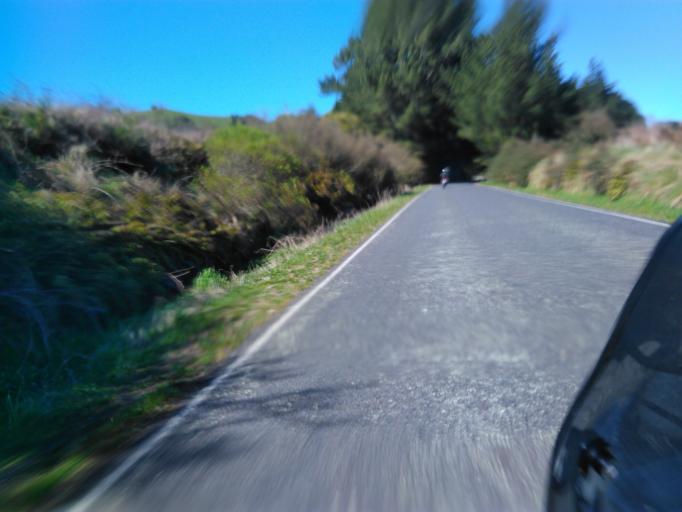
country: NZ
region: Bay of Plenty
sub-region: Opotiki District
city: Opotiki
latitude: -38.3404
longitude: 177.5346
